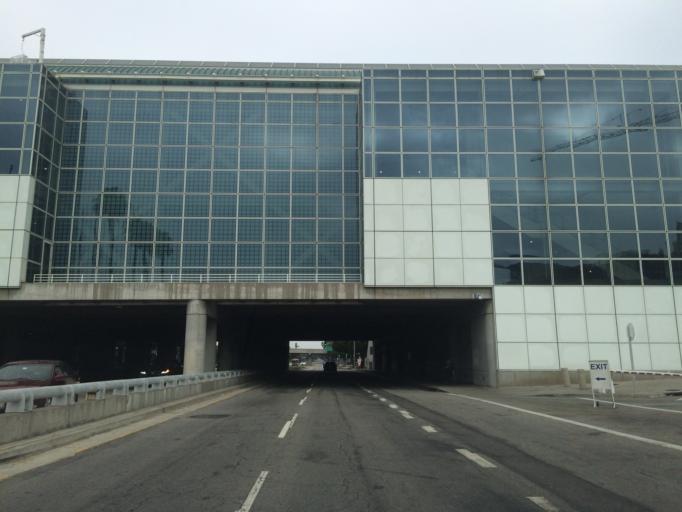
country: US
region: California
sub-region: Los Angeles County
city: Los Angeles
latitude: 34.0408
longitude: -118.2683
